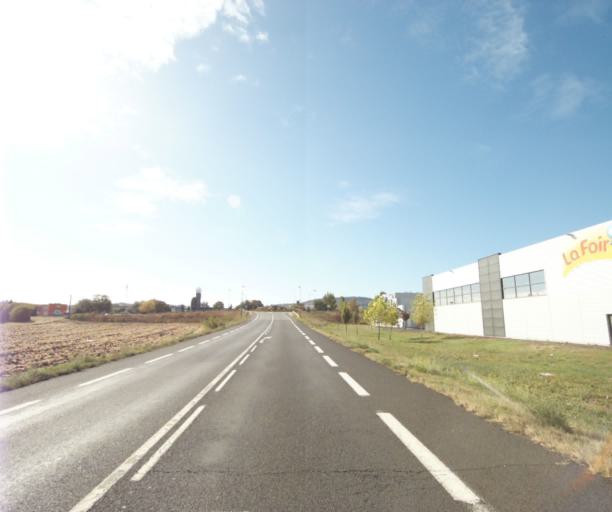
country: FR
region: Auvergne
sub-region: Departement du Puy-de-Dome
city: Malintrat
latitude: 45.7816
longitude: 3.2025
